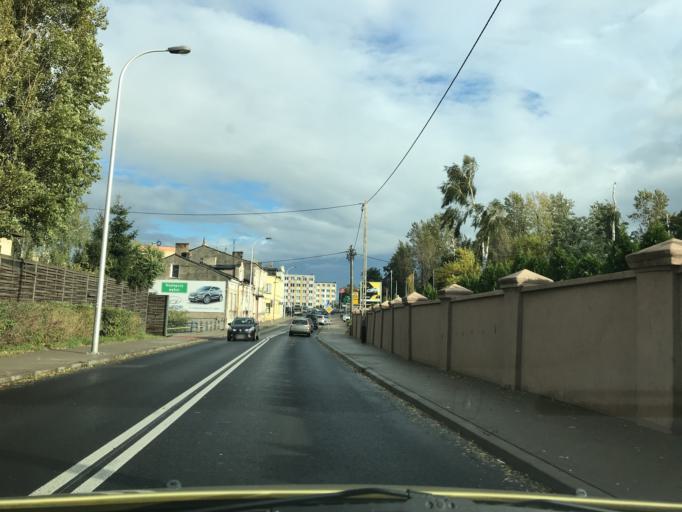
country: PL
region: Greater Poland Voivodeship
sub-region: Kalisz
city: Kalisz
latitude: 51.7611
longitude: 18.0719
